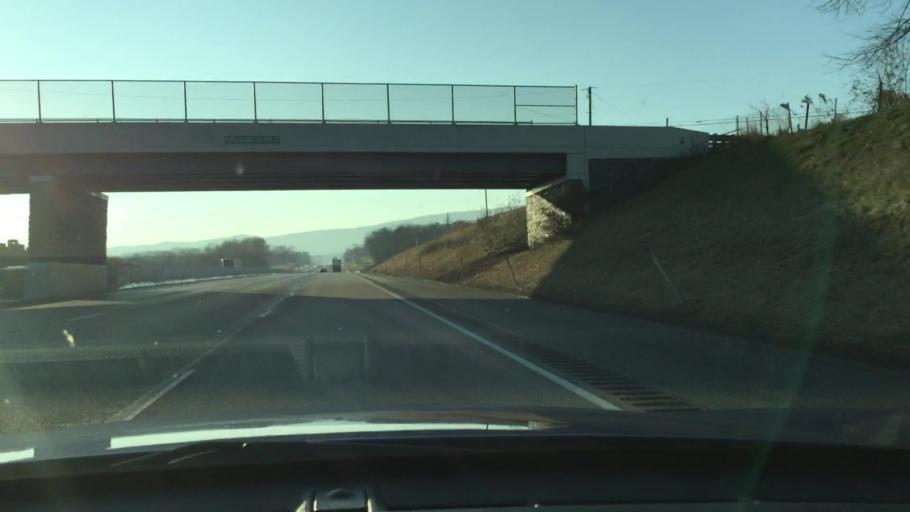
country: US
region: Pennsylvania
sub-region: Cumberland County
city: Shippensburg
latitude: 40.1713
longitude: -77.5671
